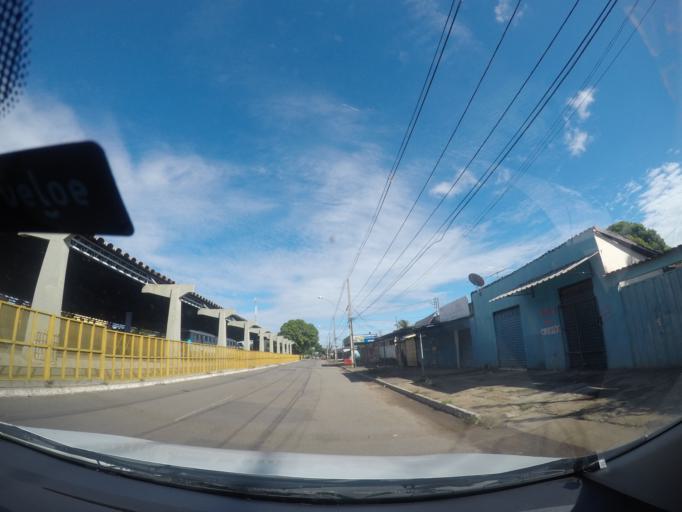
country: BR
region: Goias
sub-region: Goiania
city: Goiania
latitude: -16.6660
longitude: -49.2120
